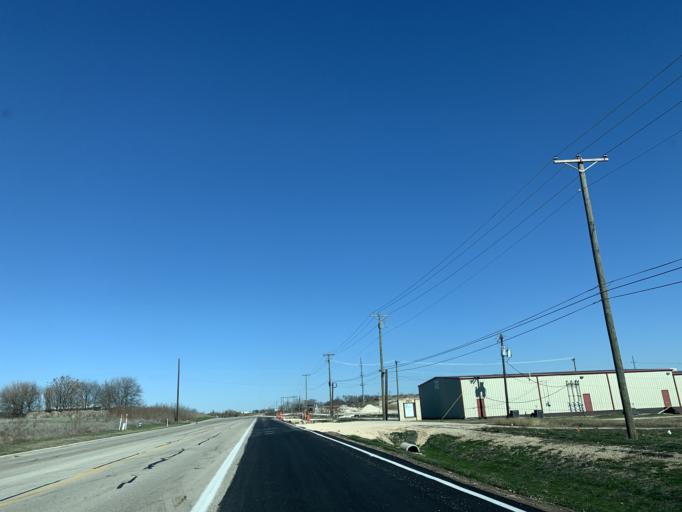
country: US
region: Texas
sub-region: Williamson County
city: Hutto
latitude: 30.5477
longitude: -97.5728
